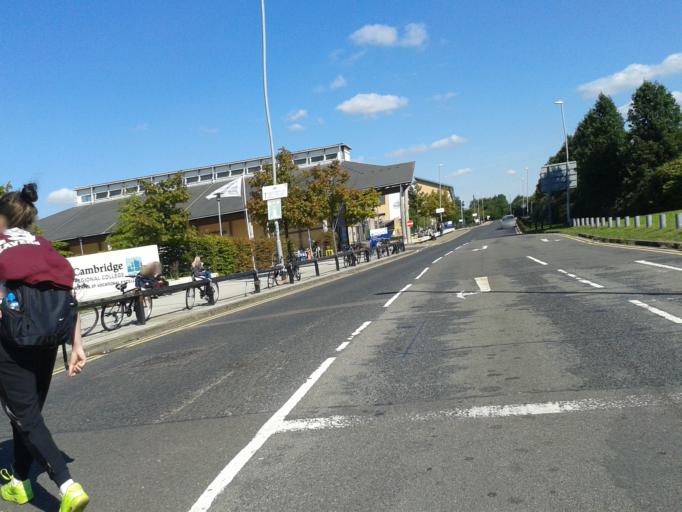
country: GB
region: England
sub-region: Cambridgeshire
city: Histon
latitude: 52.2342
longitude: 0.1351
